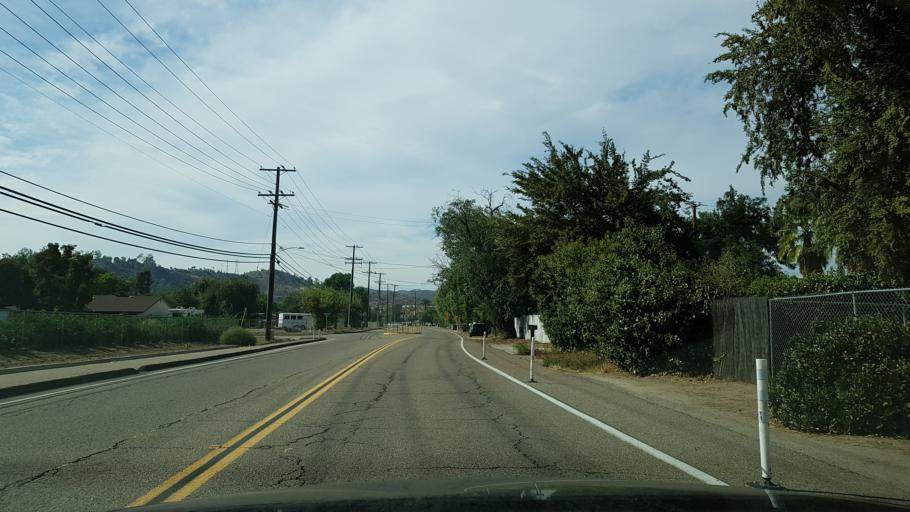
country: US
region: California
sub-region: San Diego County
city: Lakeside
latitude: 32.8758
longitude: -116.9138
